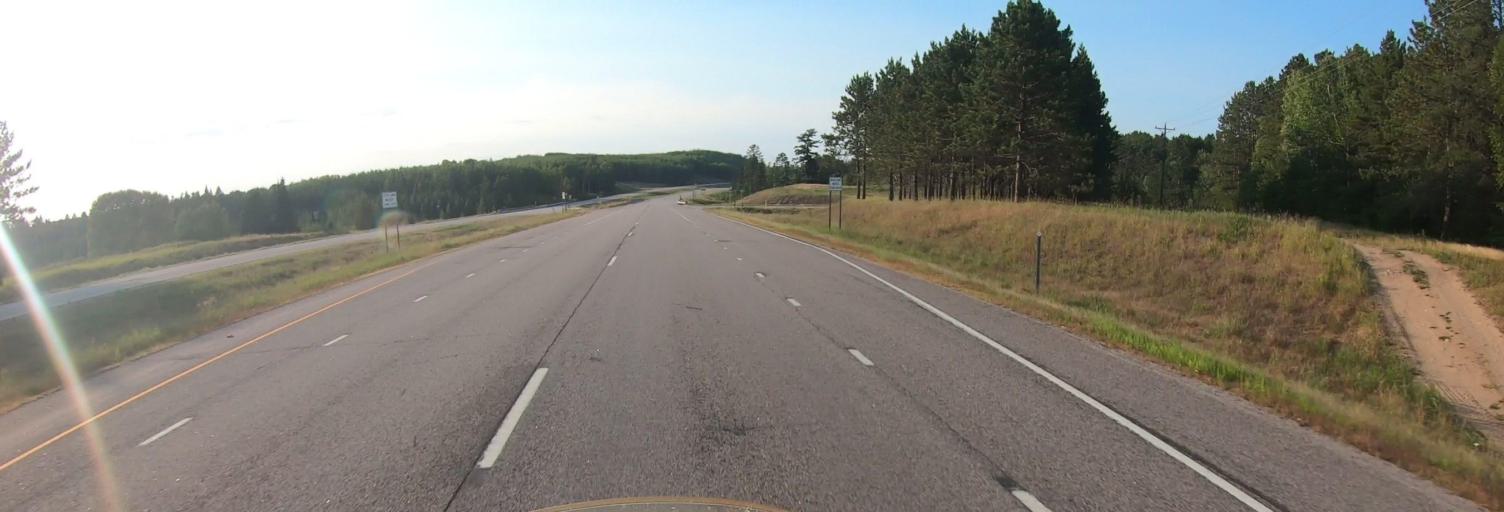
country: US
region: Minnesota
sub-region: Saint Louis County
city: Mountain Iron
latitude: 47.6765
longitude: -92.6348
